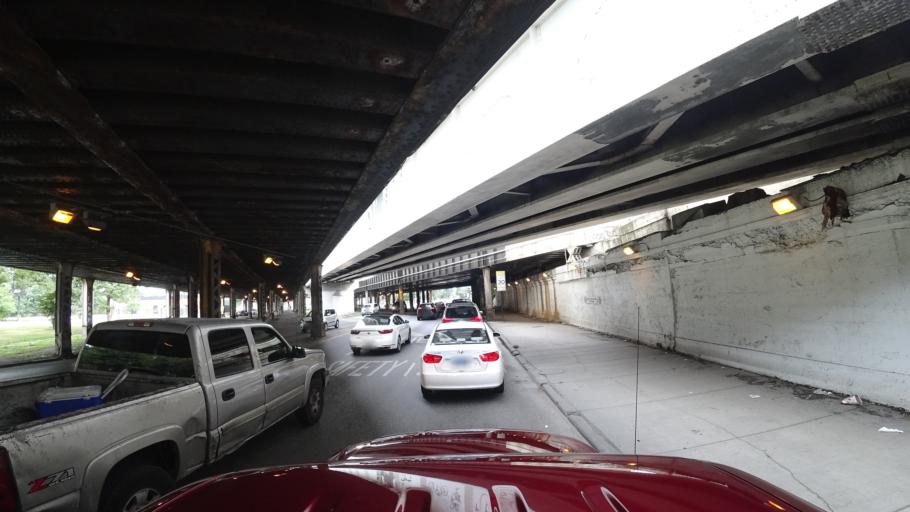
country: US
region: Illinois
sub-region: Cook County
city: Chicago
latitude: 41.8219
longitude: -87.6841
